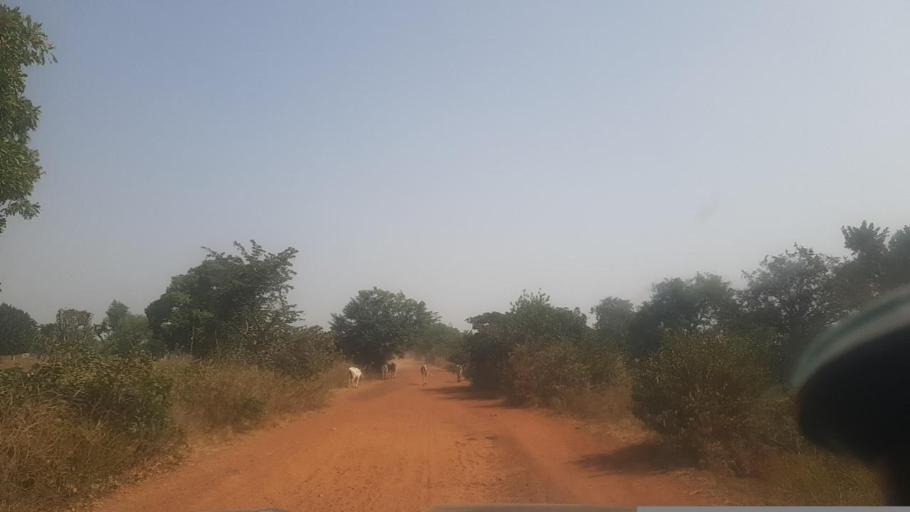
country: ML
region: Segou
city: Bla
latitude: 12.9140
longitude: -6.2488
